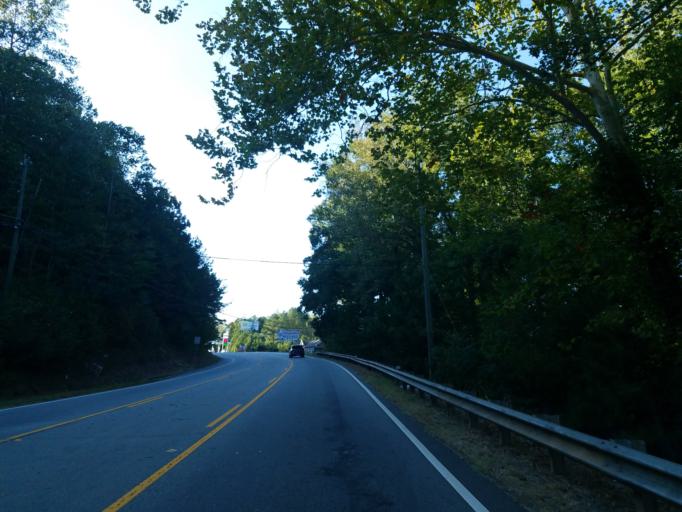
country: US
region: Georgia
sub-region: Paulding County
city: Dallas
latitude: 33.9107
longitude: -84.8167
